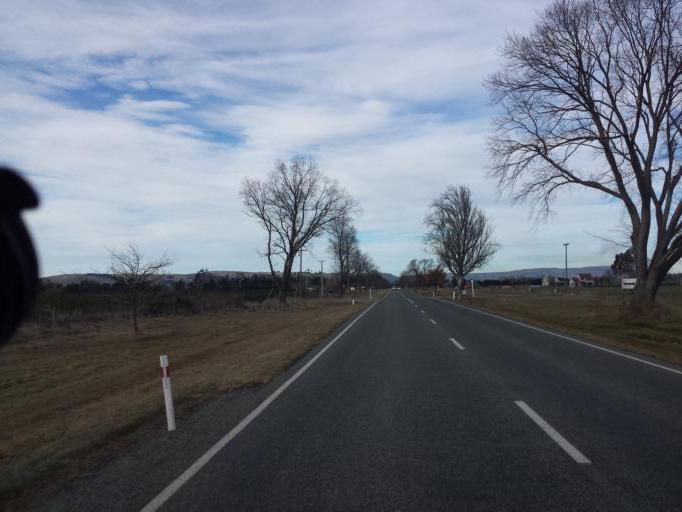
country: NZ
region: Canterbury
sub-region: Timaru District
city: Pleasant Point
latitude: -44.0727
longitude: 170.7941
